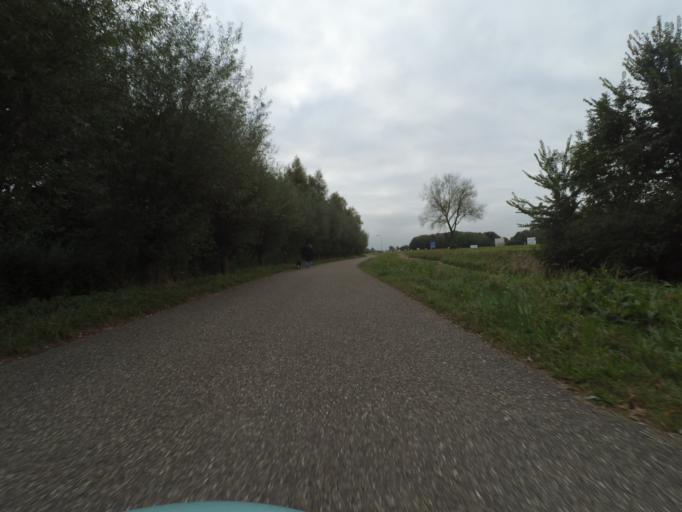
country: NL
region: Gelderland
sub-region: Gemeente Culemborg
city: Culemborg
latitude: 51.9457
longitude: 5.2783
